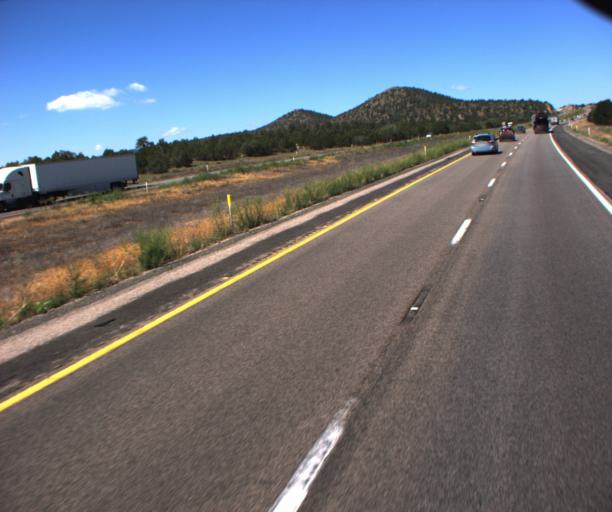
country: US
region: Arizona
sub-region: Mohave County
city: Peach Springs
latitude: 35.3030
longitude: -113.0034
